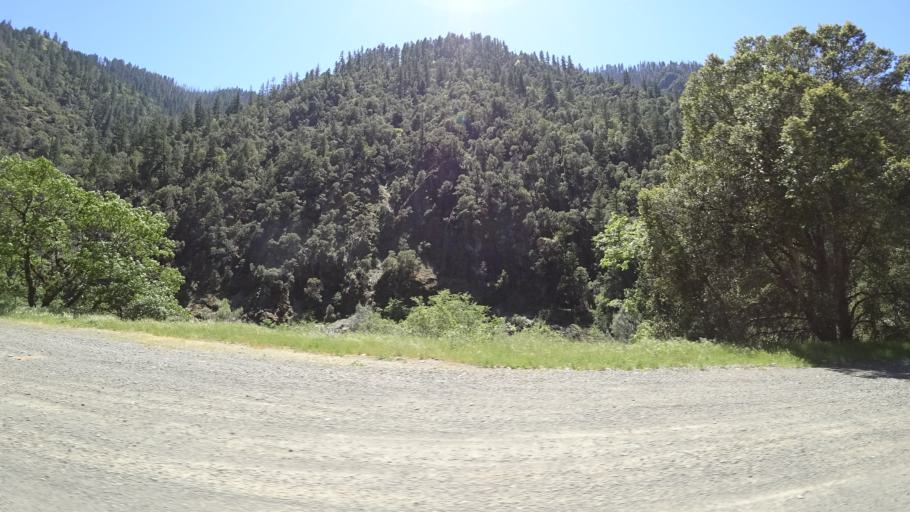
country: US
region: California
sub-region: Humboldt County
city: Willow Creek
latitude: 40.7937
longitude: -123.3738
